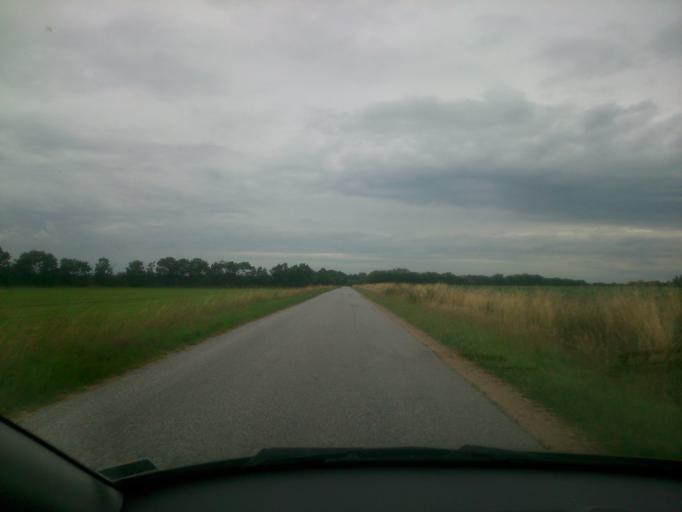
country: DK
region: South Denmark
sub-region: Varde Kommune
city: Varde
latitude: 55.5576
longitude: 8.4230
